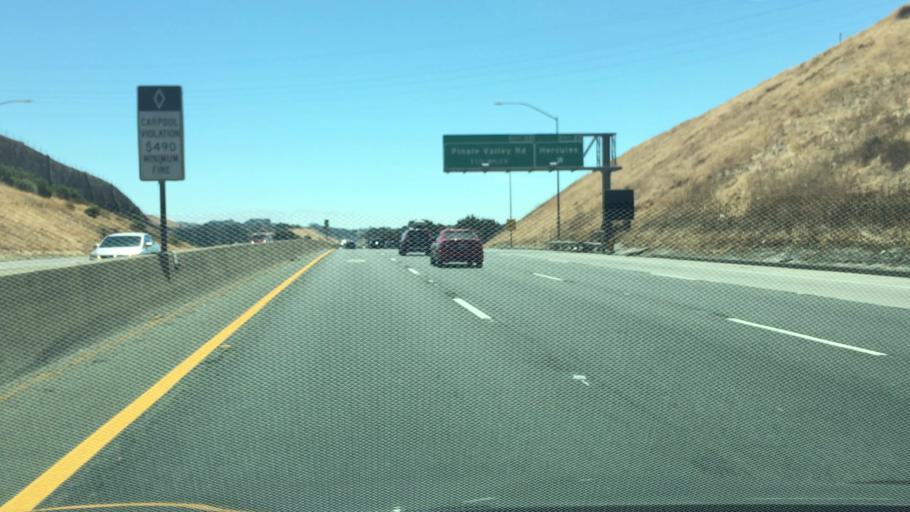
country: US
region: California
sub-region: Contra Costa County
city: Rodeo
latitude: 38.0188
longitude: -122.2662
